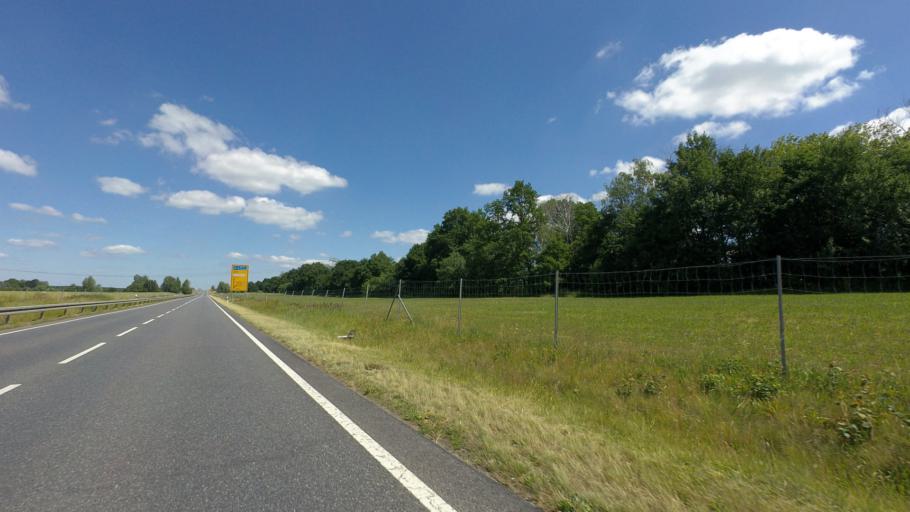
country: DE
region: Brandenburg
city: Luckau
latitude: 51.8475
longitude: 13.6831
